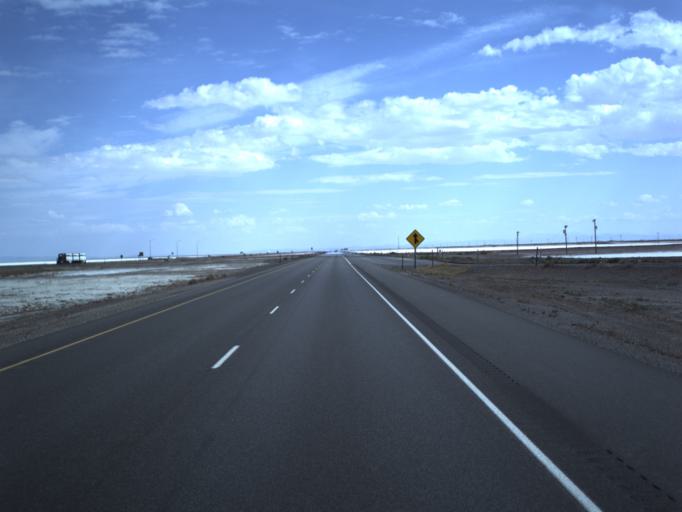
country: US
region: Utah
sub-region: Tooele County
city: Wendover
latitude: 40.7386
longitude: -113.8561
